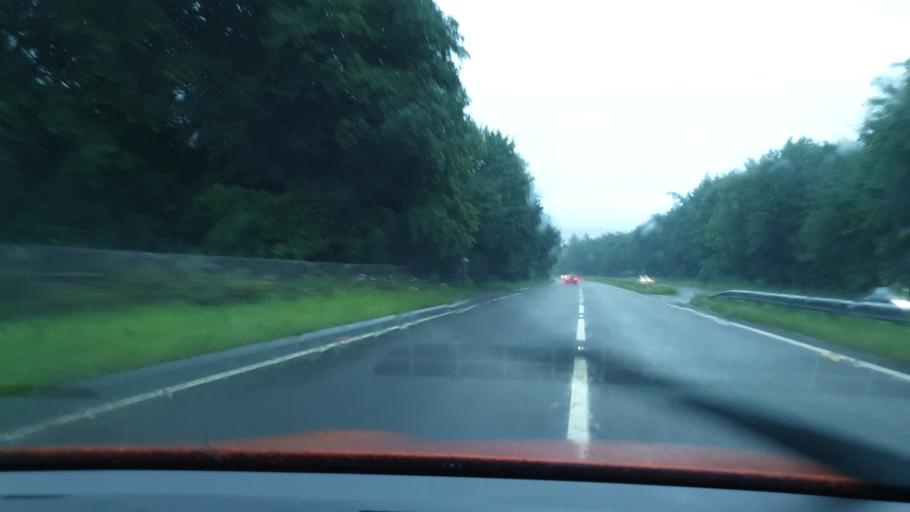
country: GB
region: England
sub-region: Cumbria
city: Grange-over-Sands
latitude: 54.2217
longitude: -2.9041
